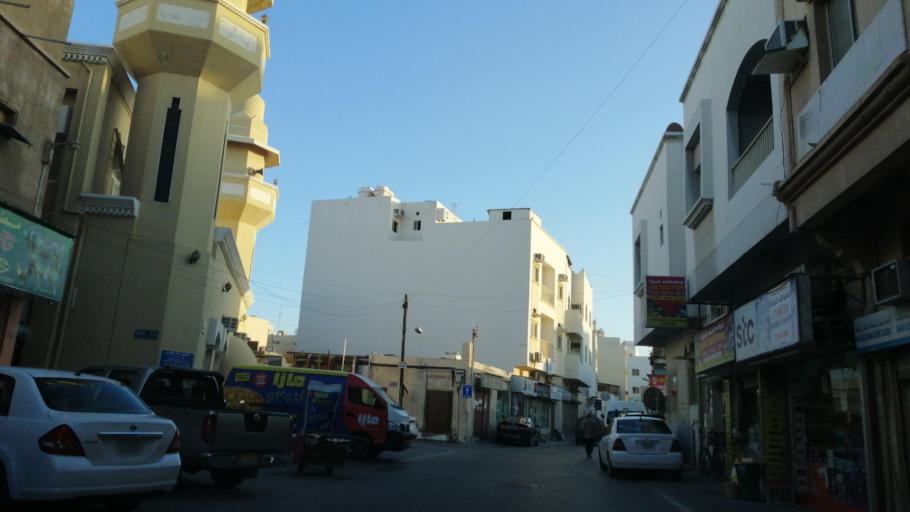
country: BH
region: Muharraq
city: Al Hadd
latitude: 26.2433
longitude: 50.6539
